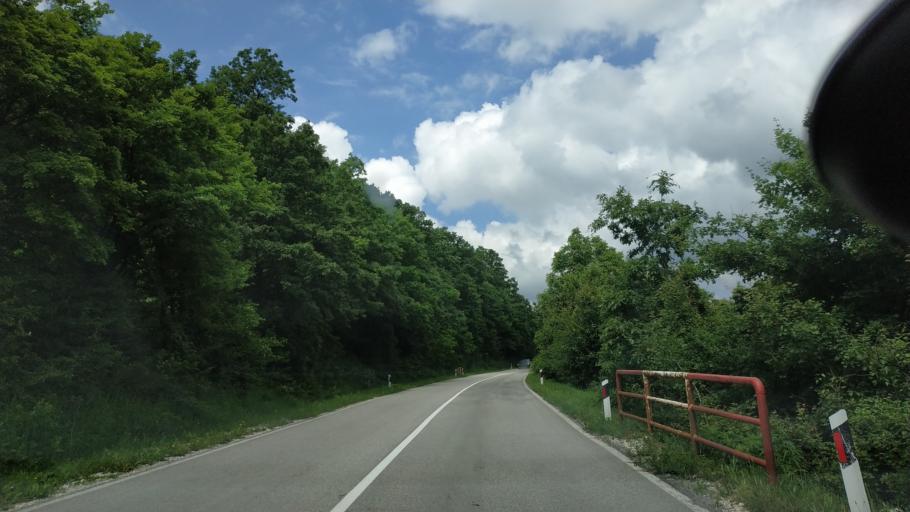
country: RS
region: Central Serbia
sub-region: Borski Okrug
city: Bor
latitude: 44.0627
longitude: 22.0387
